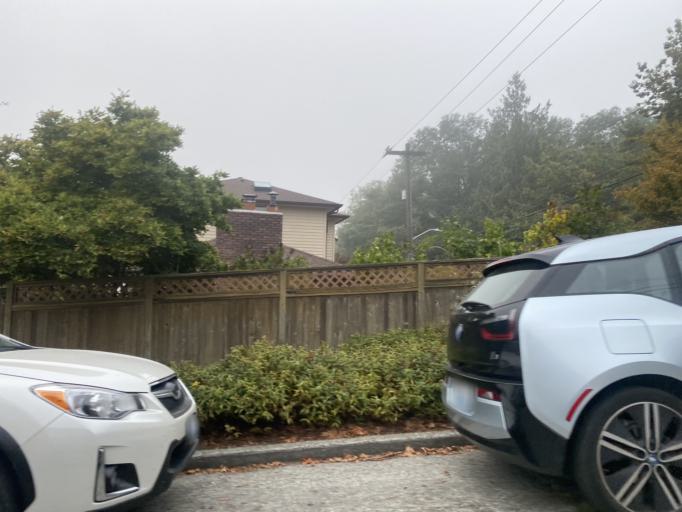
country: US
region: Washington
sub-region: King County
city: Seattle
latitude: 47.6539
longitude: -122.4133
